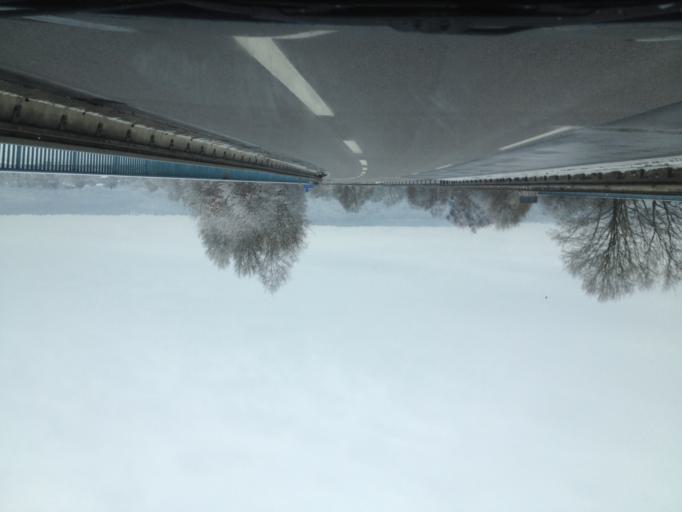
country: DE
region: Rheinland-Pfalz
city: Zweibrucken
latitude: 49.2642
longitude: 7.3147
